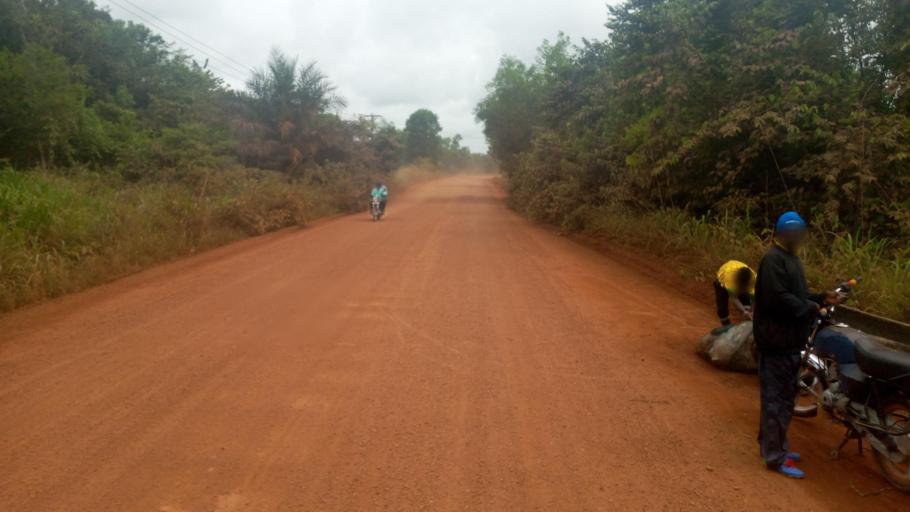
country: SL
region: Southern Province
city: Mogbwemo
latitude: 7.7466
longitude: -12.2921
